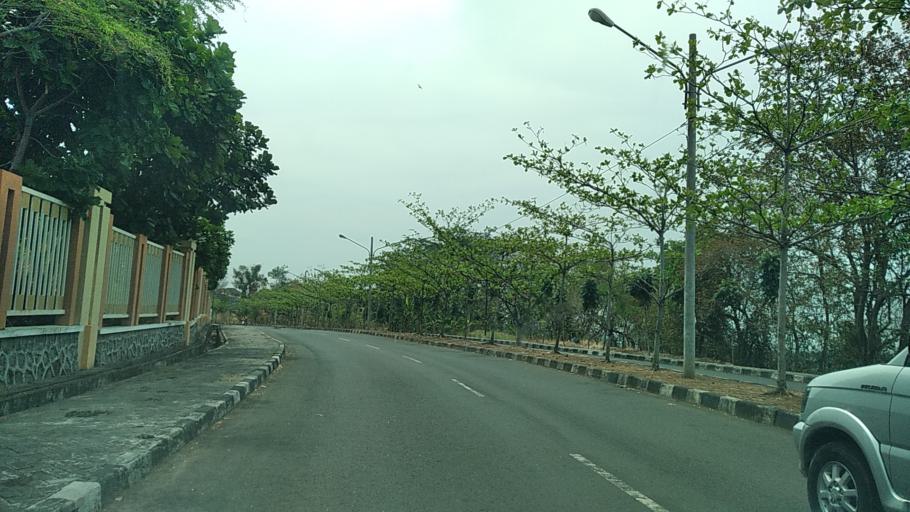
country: ID
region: Central Java
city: Semarang
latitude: -7.0466
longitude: 110.4432
